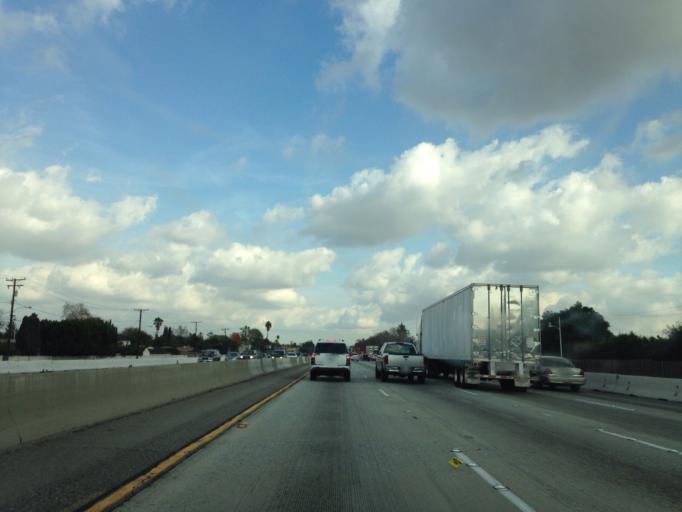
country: US
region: California
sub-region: Los Angeles County
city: Baldwin Park
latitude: 34.0709
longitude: -117.9556
